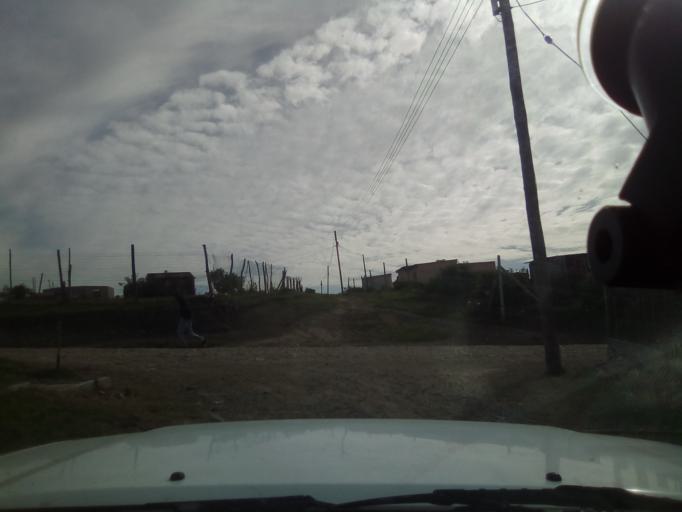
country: ZA
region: Eastern Cape
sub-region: Amathole District Municipality
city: Komga
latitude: -32.7924
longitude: 27.9620
